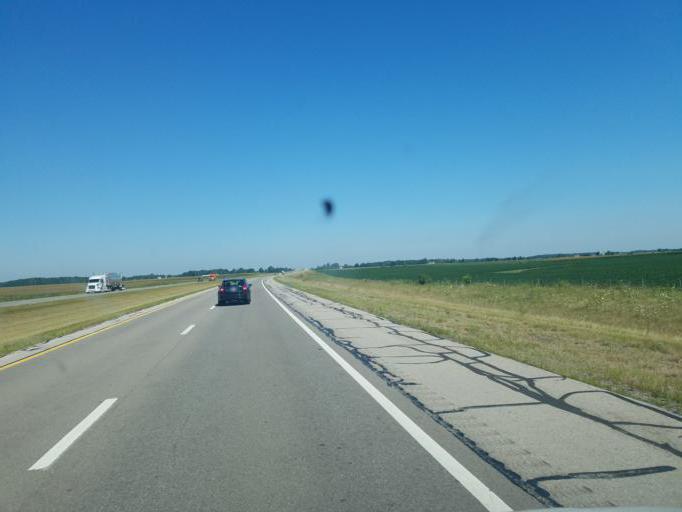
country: US
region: Ohio
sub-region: Crawford County
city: Bucyrus
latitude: 40.7863
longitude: -82.9046
